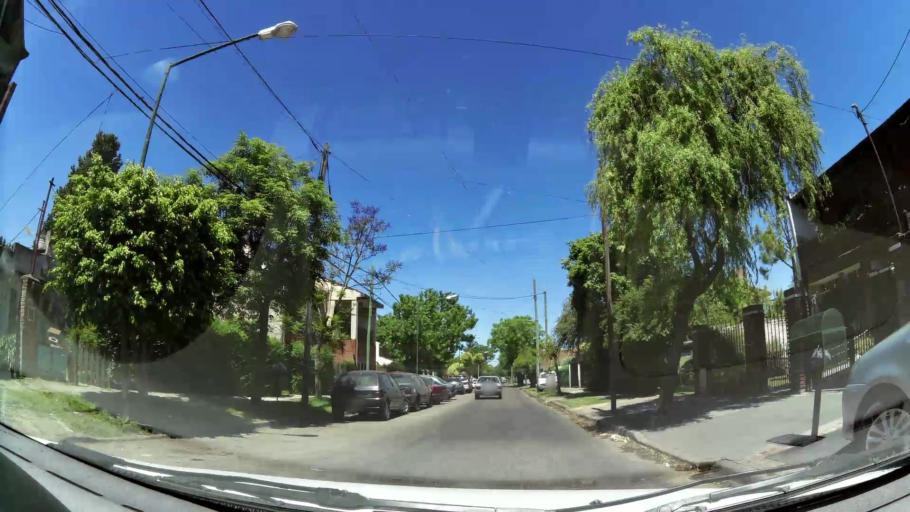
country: AR
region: Buenos Aires
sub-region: Partido de San Isidro
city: San Isidro
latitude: -34.5040
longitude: -58.5717
